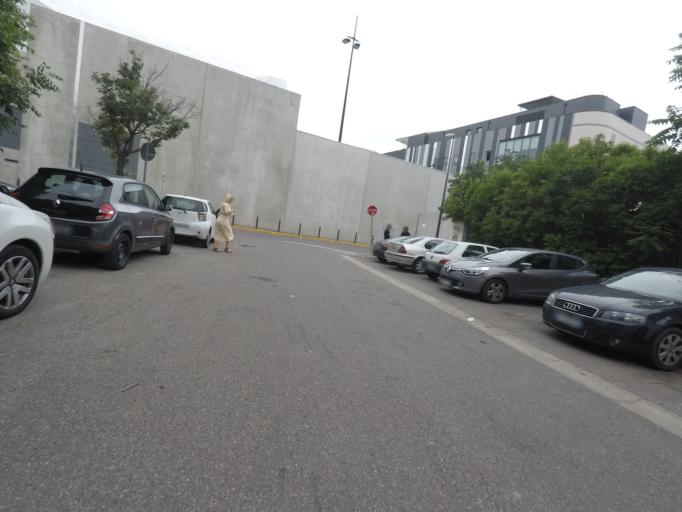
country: FR
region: Provence-Alpes-Cote d'Azur
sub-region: Departement des Bouches-du-Rhone
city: Marseille 08
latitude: 43.2712
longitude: 5.3942
